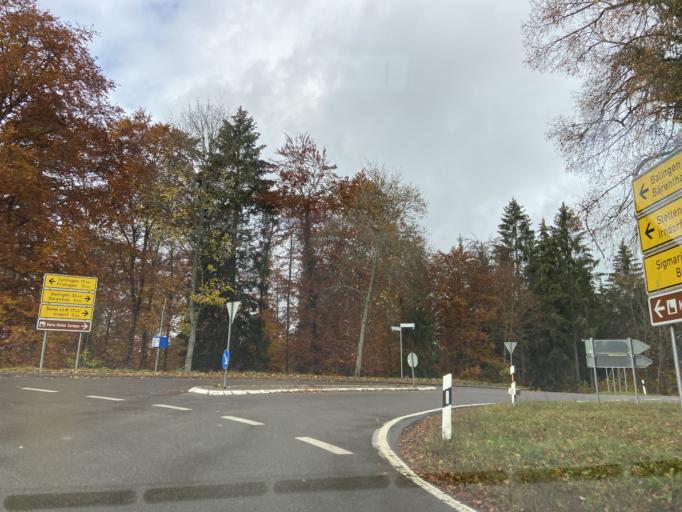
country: DE
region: Baden-Wuerttemberg
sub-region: Tuebingen Region
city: Beuron
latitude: 48.0473
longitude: 8.9517
